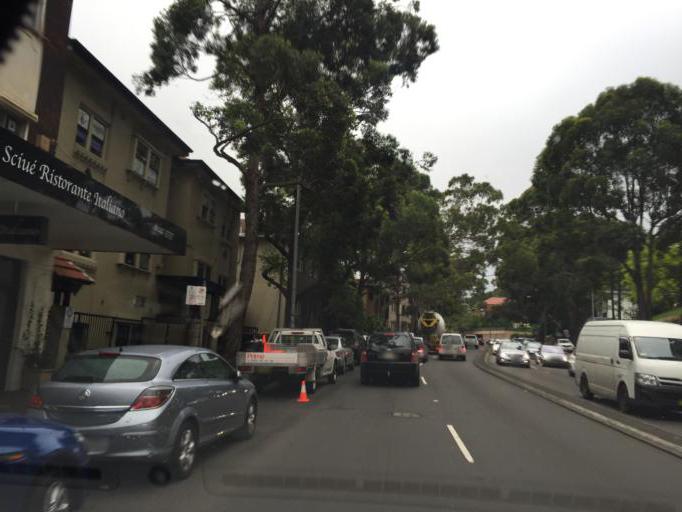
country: AU
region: New South Wales
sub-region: Woollahra
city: Bellevue Hill
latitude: -33.8768
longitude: 151.2452
